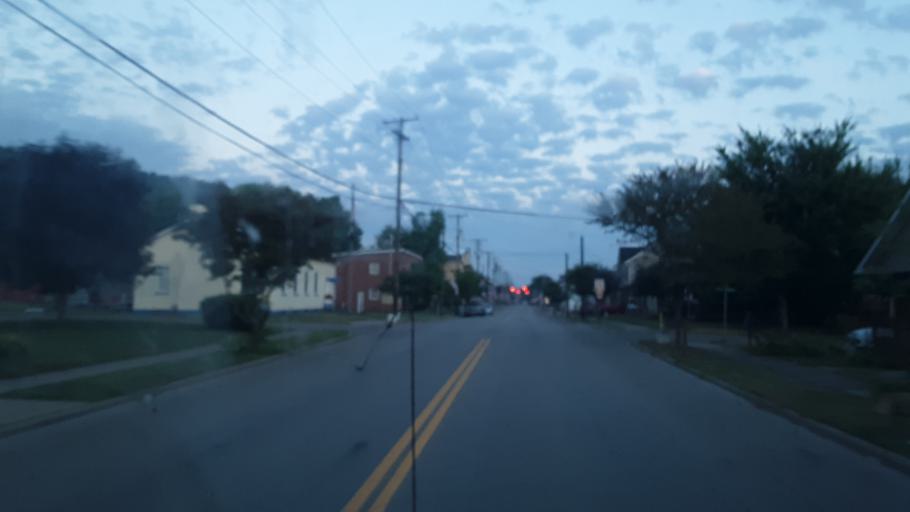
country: US
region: Ohio
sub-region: Carroll County
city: Lake Mohawk
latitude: 40.6681
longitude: -81.2543
